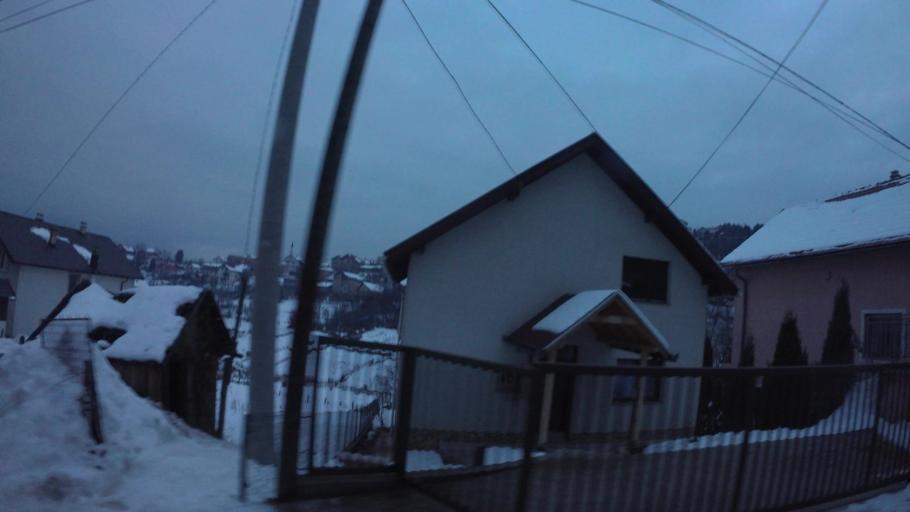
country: BA
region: Federation of Bosnia and Herzegovina
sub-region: Kanton Sarajevo
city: Sarajevo
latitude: 43.8550
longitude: 18.3413
